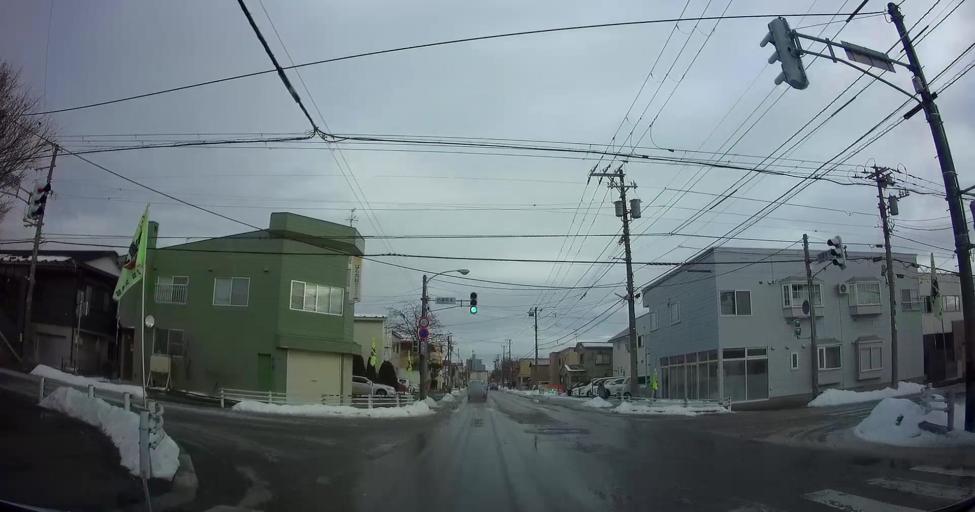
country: JP
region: Hokkaido
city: Hakodate
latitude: 41.7781
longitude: 140.7475
